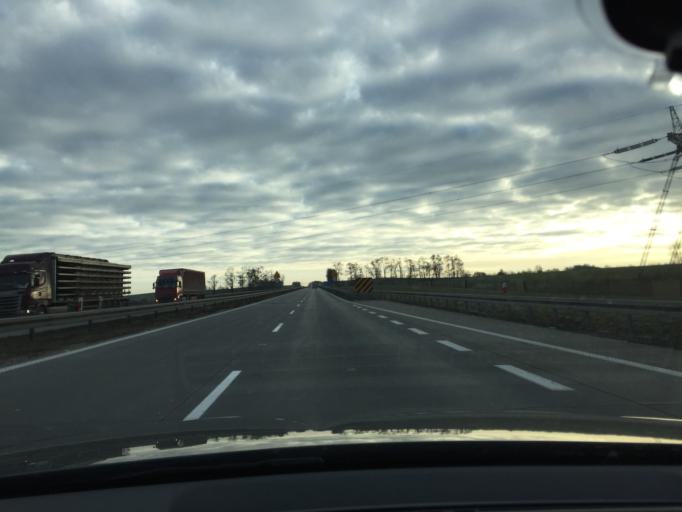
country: PL
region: Lower Silesian Voivodeship
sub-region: Powiat legnicki
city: Legnickie Pole
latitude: 51.1396
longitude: 16.2837
